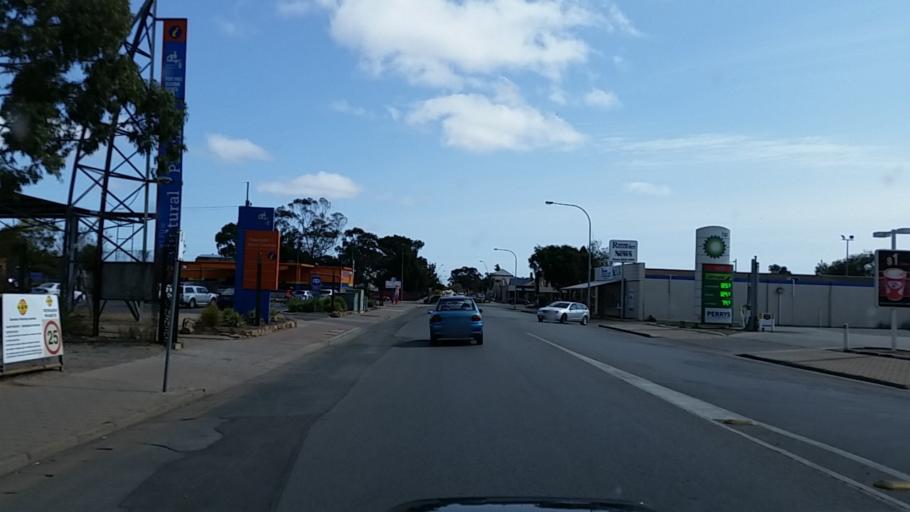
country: AU
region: South Australia
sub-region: Port Pirie City and Dists
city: Port Pirie
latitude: -33.1803
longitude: 138.0117
